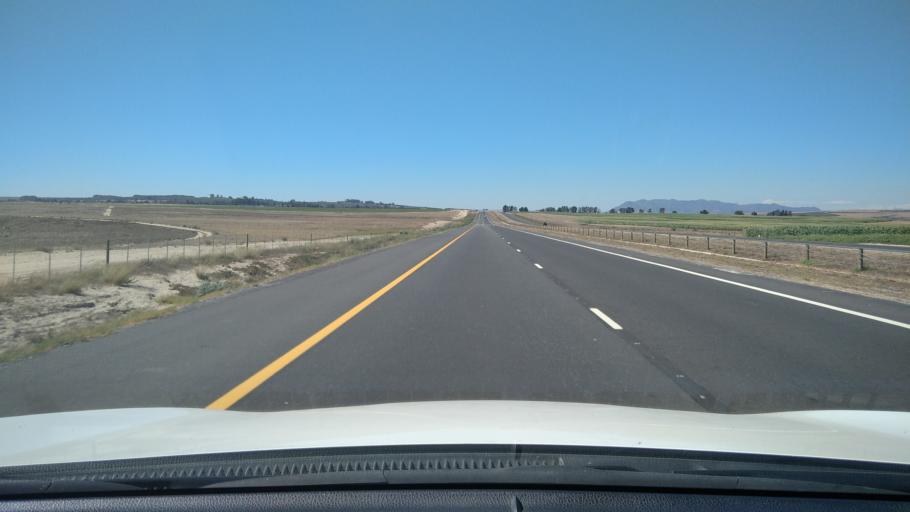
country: ZA
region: Western Cape
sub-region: West Coast District Municipality
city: Malmesbury
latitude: -33.5470
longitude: 18.6345
